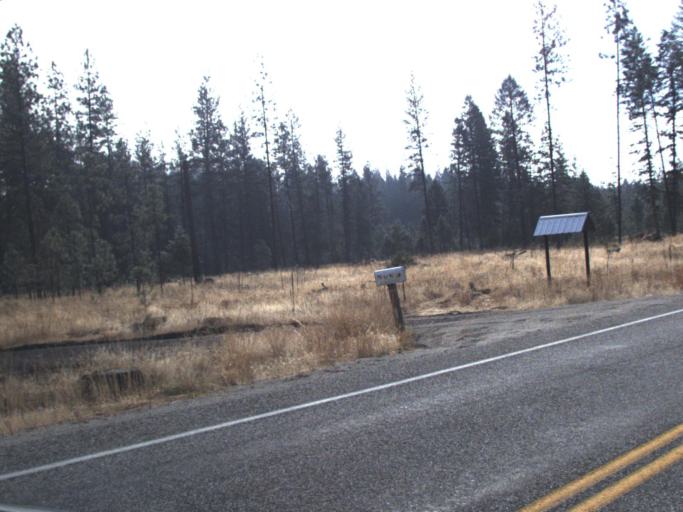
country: US
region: Washington
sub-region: Stevens County
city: Kettle Falls
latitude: 48.7853
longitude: -118.1487
